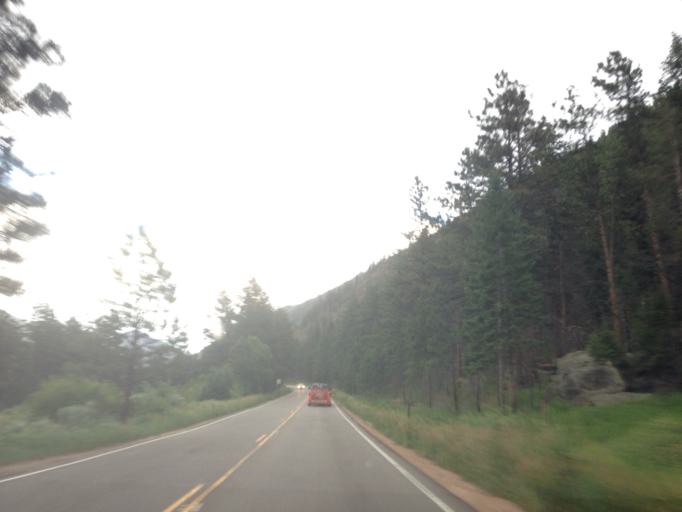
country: US
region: Colorado
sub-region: Larimer County
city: Laporte
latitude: 40.6877
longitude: -105.3576
